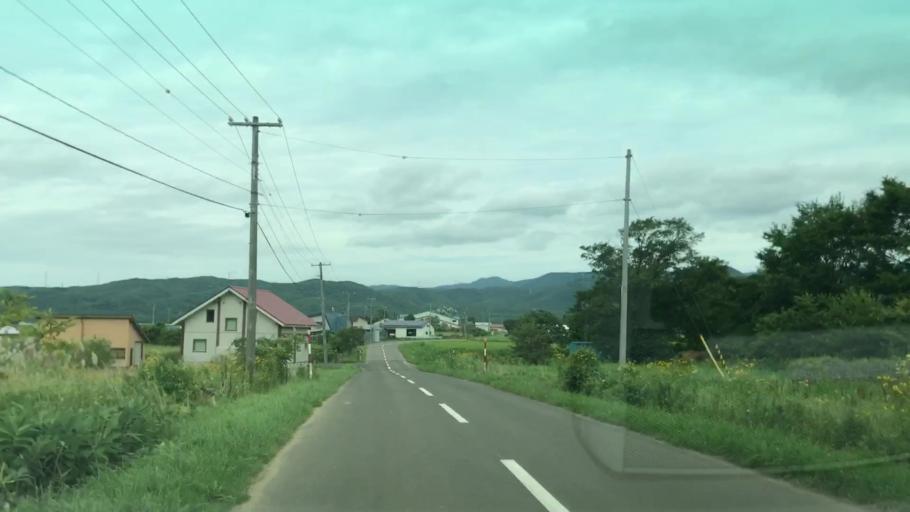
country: JP
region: Hokkaido
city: Iwanai
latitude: 43.0264
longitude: 140.5687
